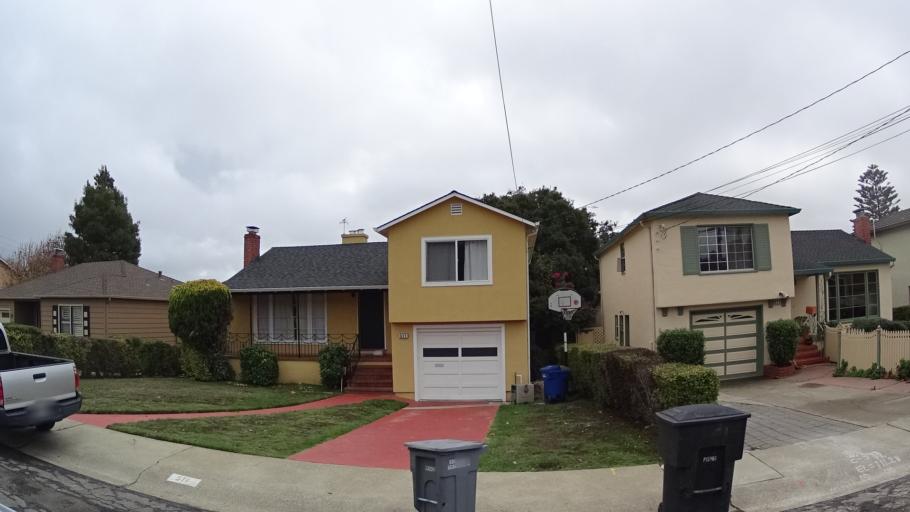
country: US
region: California
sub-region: San Mateo County
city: San Bruno
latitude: 37.6116
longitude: -122.4134
